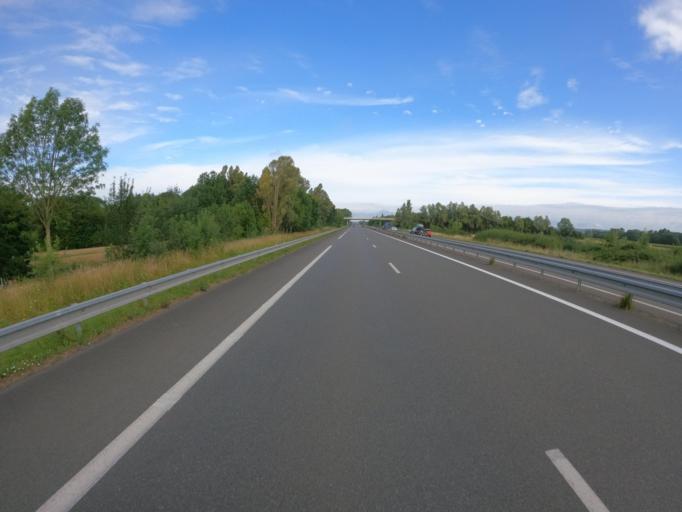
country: FR
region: Centre
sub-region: Departement d'Indre-et-Loire
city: Saint-Nicolas-de-Bourgueil
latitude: 47.2657
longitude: 0.1216
